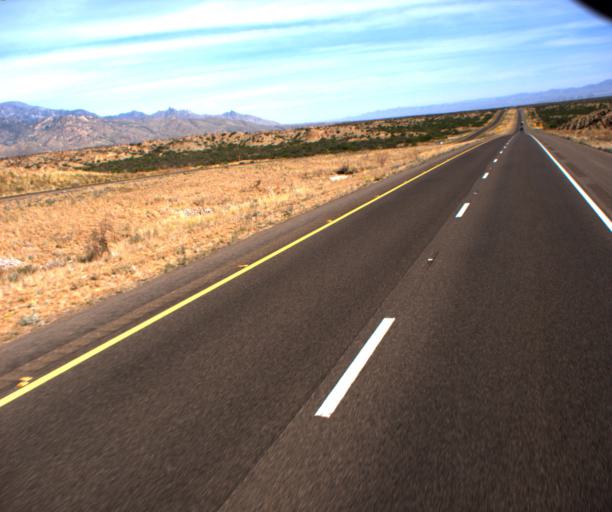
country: US
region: Arizona
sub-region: Graham County
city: Swift Trail Junction
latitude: 32.5785
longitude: -109.6819
